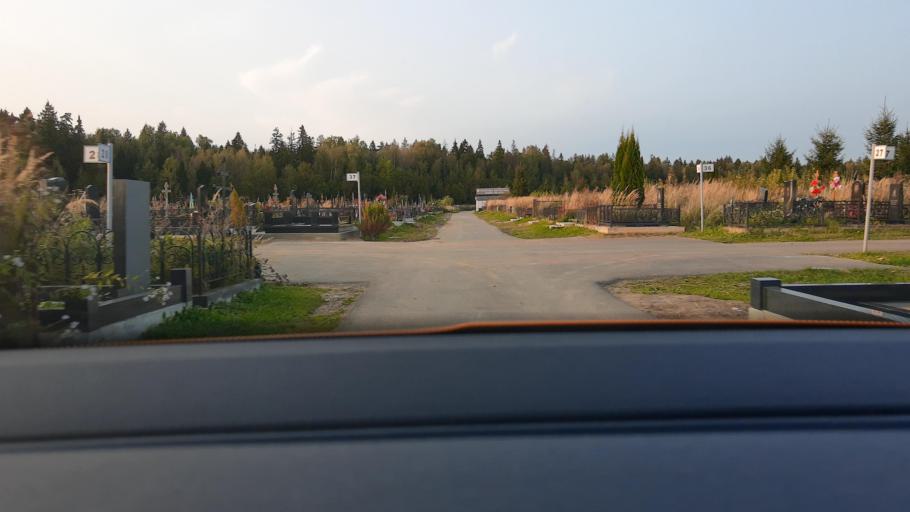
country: RU
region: Moskovskaya
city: Novopodrezkovo
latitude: 56.0092
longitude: 37.3823
